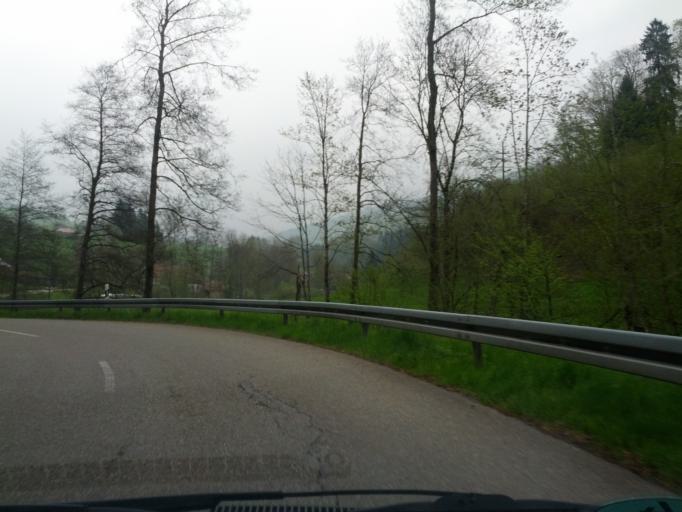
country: DE
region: Baden-Wuerttemberg
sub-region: Freiburg Region
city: Zell im Wiesental
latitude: 47.7343
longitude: 7.8073
